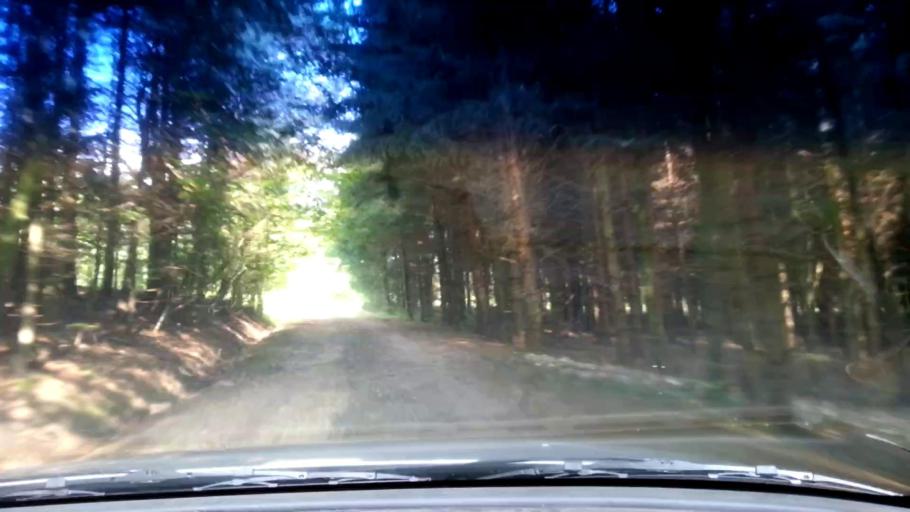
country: DE
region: Bavaria
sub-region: Upper Franconia
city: Gundelsheim
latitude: 49.9724
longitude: 10.9408
